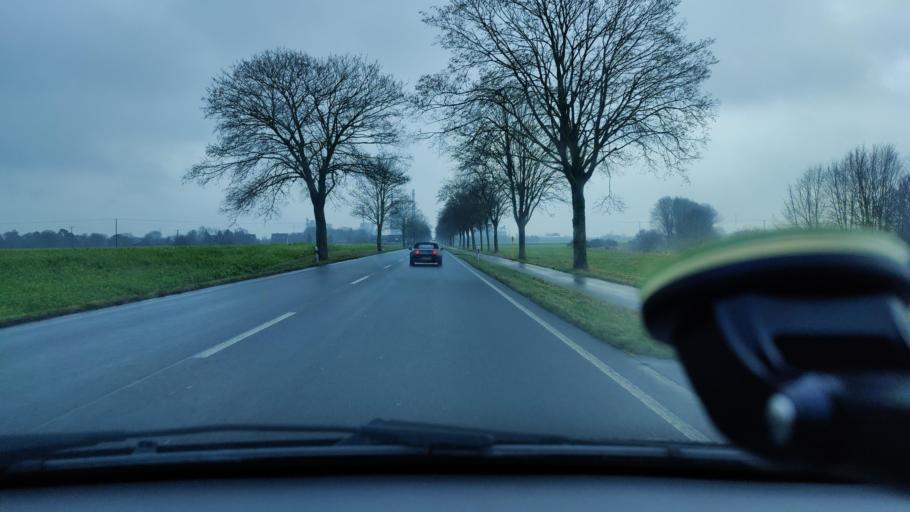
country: DE
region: North Rhine-Westphalia
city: Rheinberg
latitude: 51.5732
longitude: 6.5655
